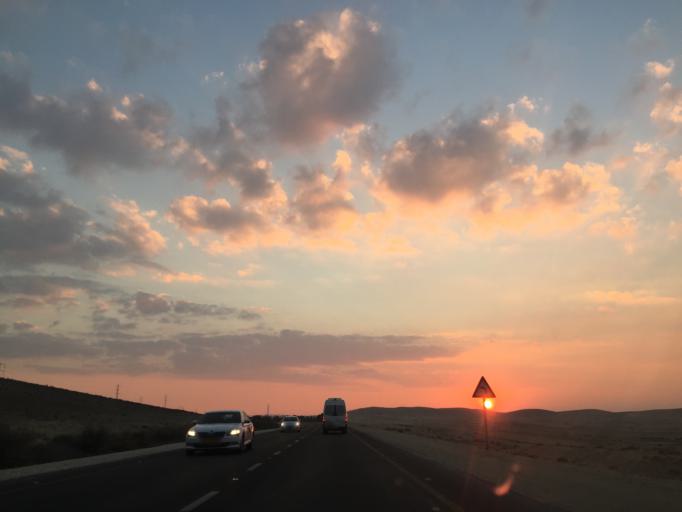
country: IL
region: Southern District
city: Yeroham
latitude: 31.0358
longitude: 34.8050
